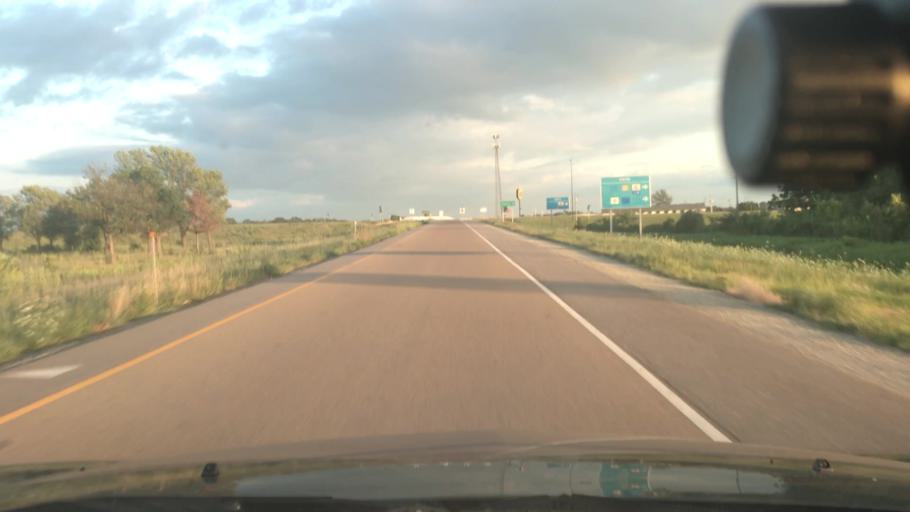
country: US
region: Illinois
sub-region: Washington County
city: Okawville
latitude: 38.4406
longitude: -89.5336
